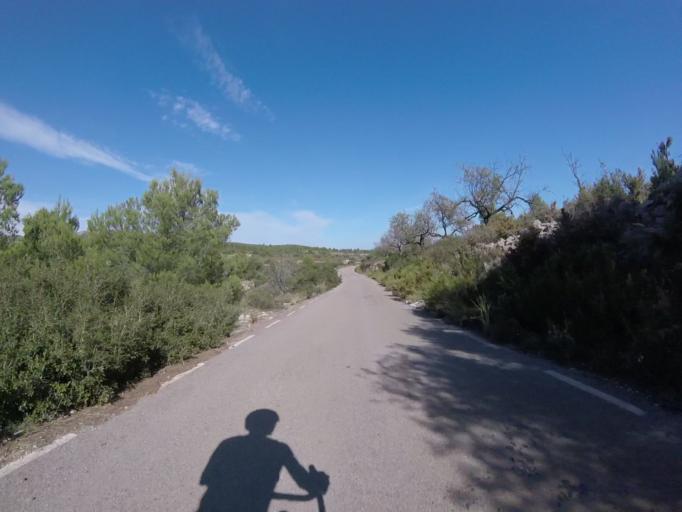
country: ES
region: Valencia
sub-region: Provincia de Castello
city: Sarratella
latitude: 40.2789
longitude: 0.0614
